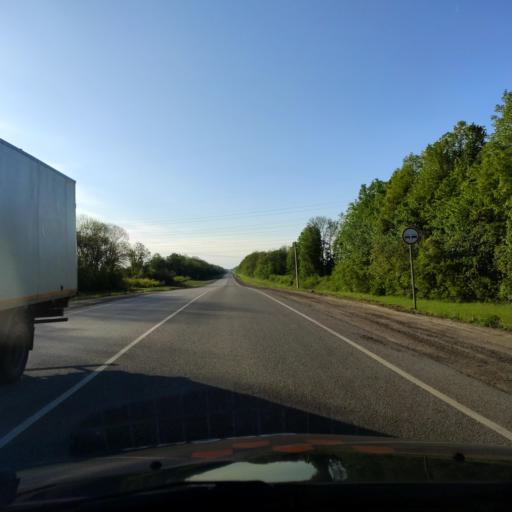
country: RU
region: Lipetsk
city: Yelets
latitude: 52.5781
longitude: 38.6417
